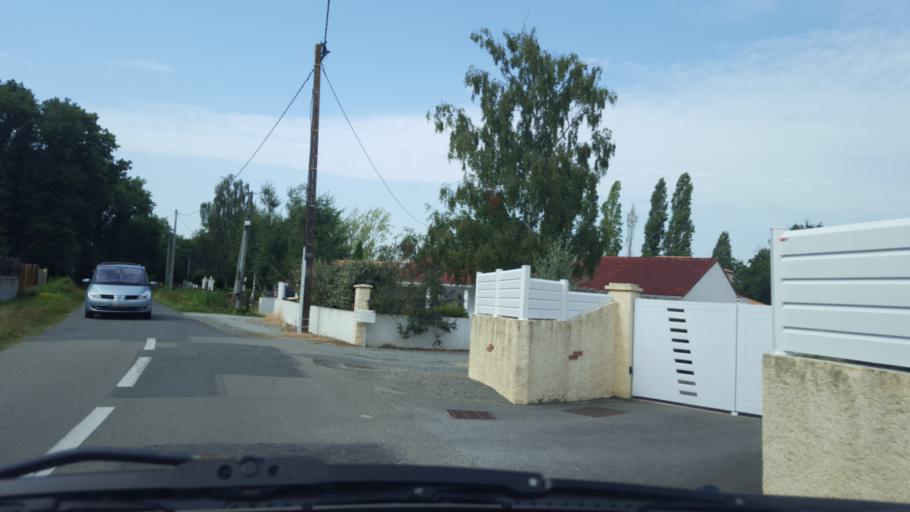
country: FR
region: Pays de la Loire
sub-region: Departement de la Loire-Atlantique
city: Saint-Philbert-de-Grand-Lieu
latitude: 47.0072
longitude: -1.6325
